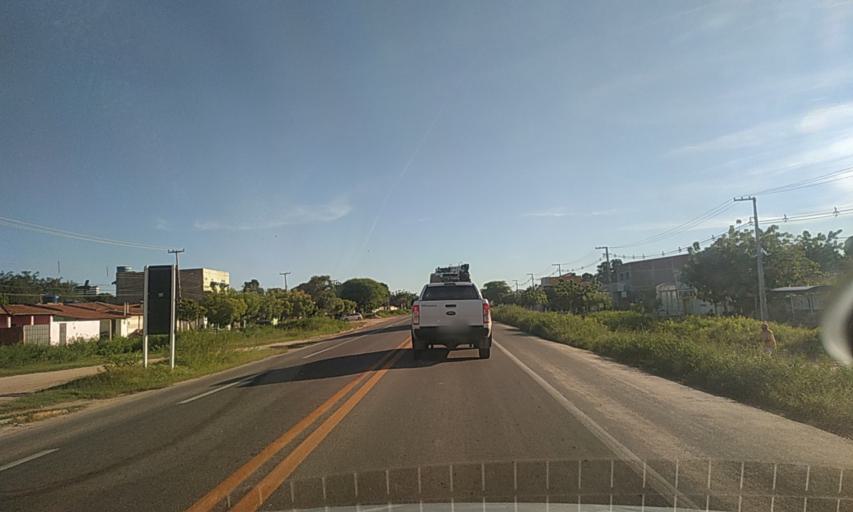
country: BR
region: Rio Grande do Norte
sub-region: Mossoro
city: Mossoro
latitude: -5.1968
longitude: -37.3169
